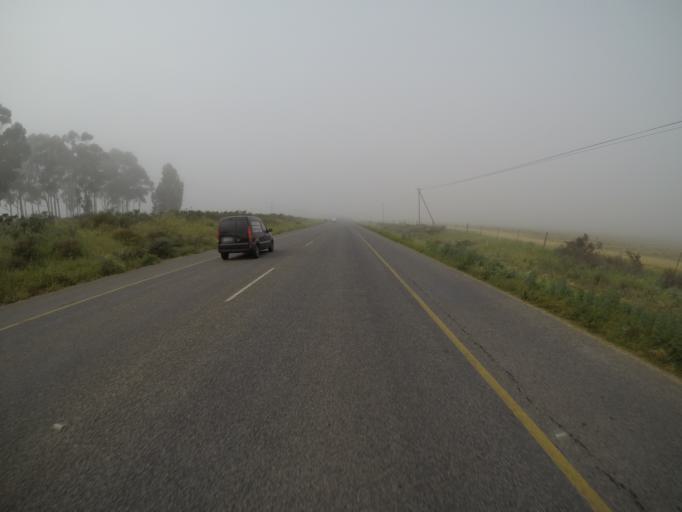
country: ZA
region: Western Cape
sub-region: City of Cape Town
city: Kraaifontein
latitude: -33.6850
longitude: 18.7050
